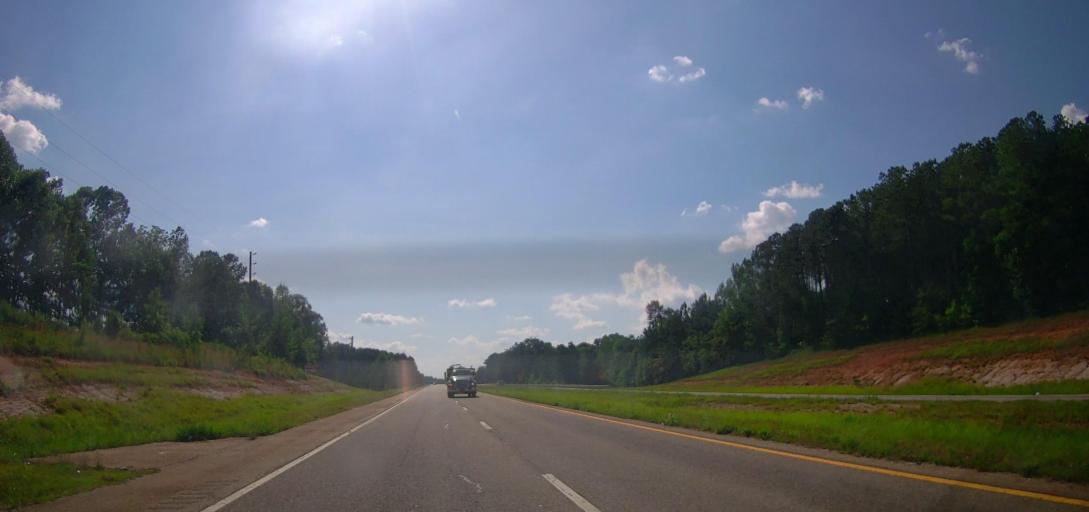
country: US
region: Georgia
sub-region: Henry County
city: Hampton
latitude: 33.3772
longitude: -84.2726
